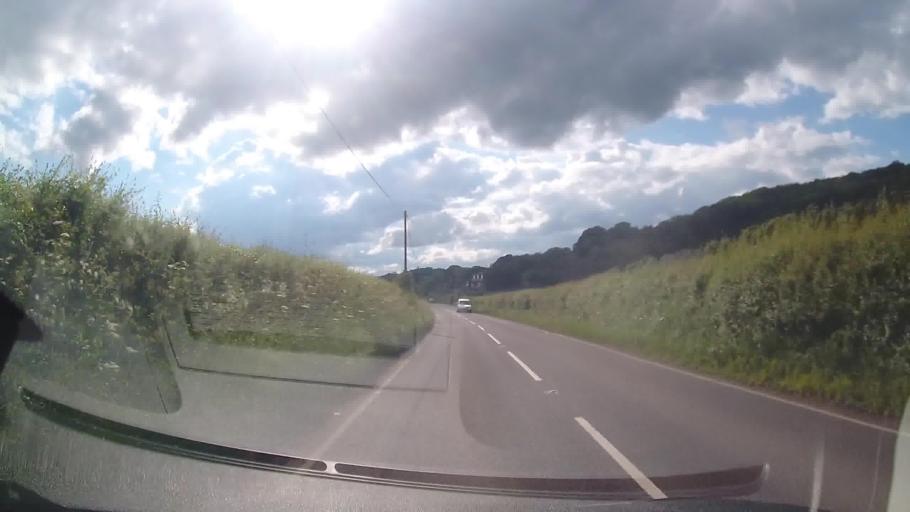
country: GB
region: England
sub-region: Shropshire
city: Much Wenlock
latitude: 52.6405
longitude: -2.5415
